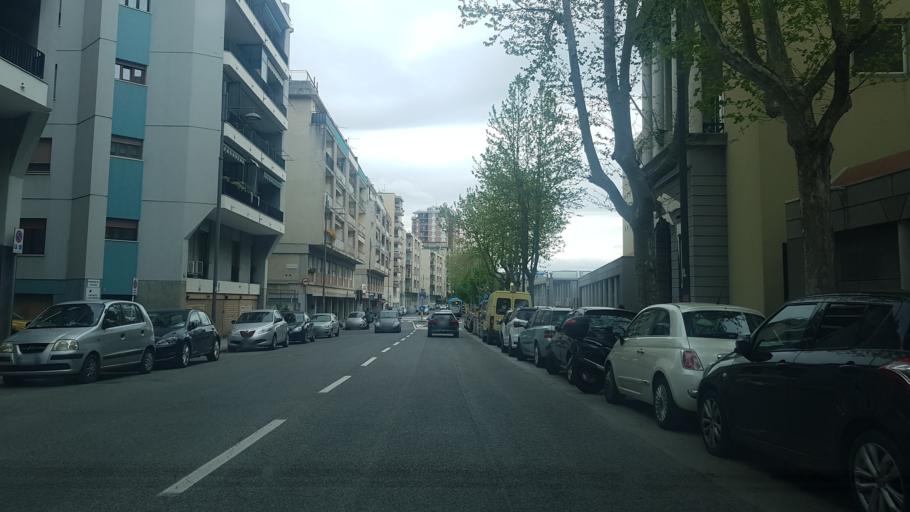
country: IT
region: Friuli Venezia Giulia
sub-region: Provincia di Trieste
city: Trieste
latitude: 45.6414
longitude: 13.7609
